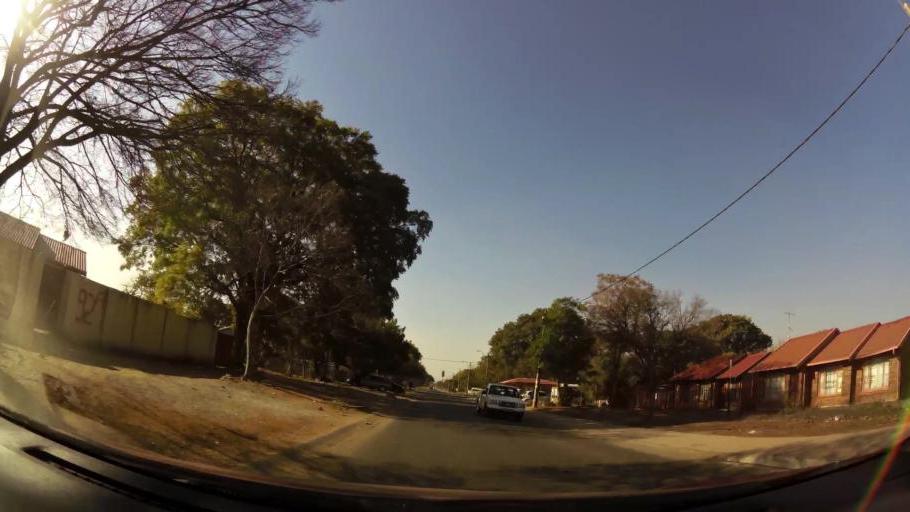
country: ZA
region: North-West
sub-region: Bojanala Platinum District Municipality
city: Rustenburg
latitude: -25.6562
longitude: 27.2287
